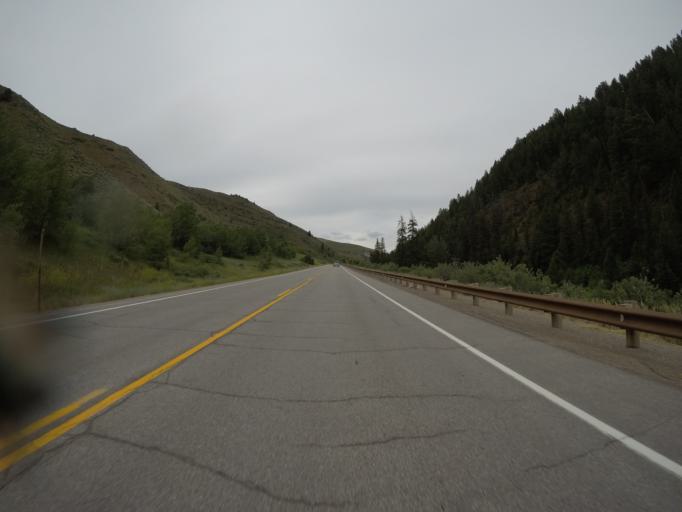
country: US
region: Wyoming
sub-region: Lincoln County
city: Afton
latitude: 42.4882
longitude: -110.9538
